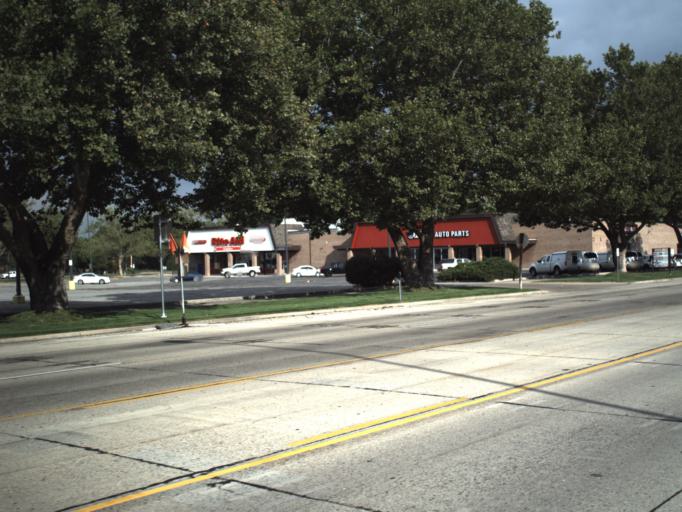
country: US
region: Utah
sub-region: Weber County
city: Harrisville
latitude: 41.2607
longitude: -111.9695
